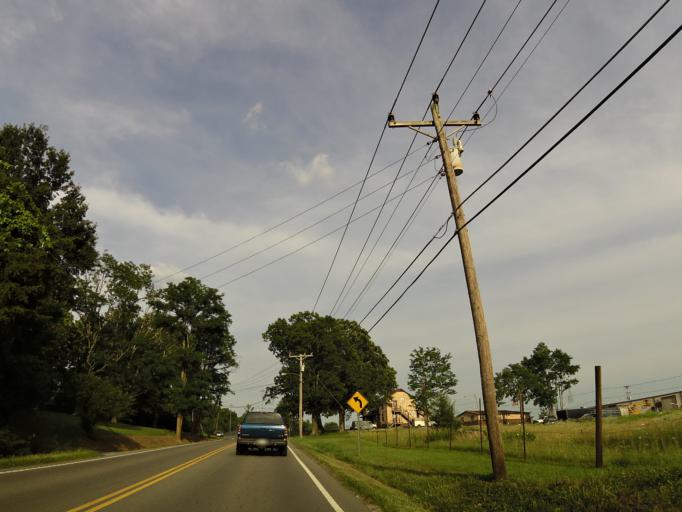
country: US
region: Tennessee
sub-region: Dickson County
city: Dickson
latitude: 36.0642
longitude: -87.3569
